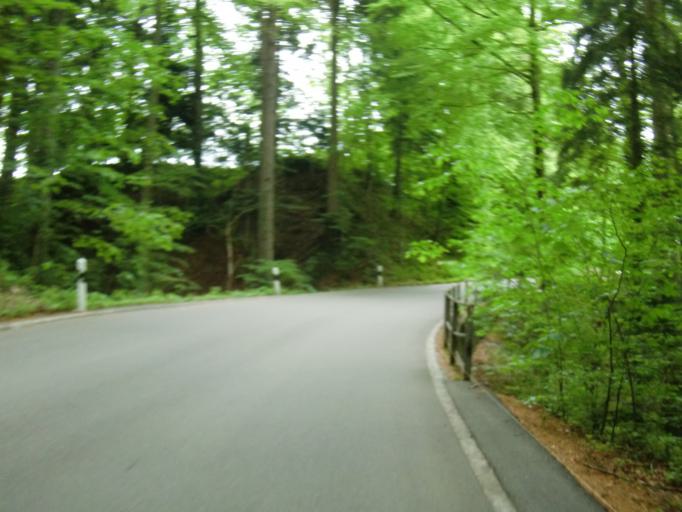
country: CH
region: Zurich
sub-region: Bezirk Hinwil
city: Wald
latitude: 47.2781
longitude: 8.8910
